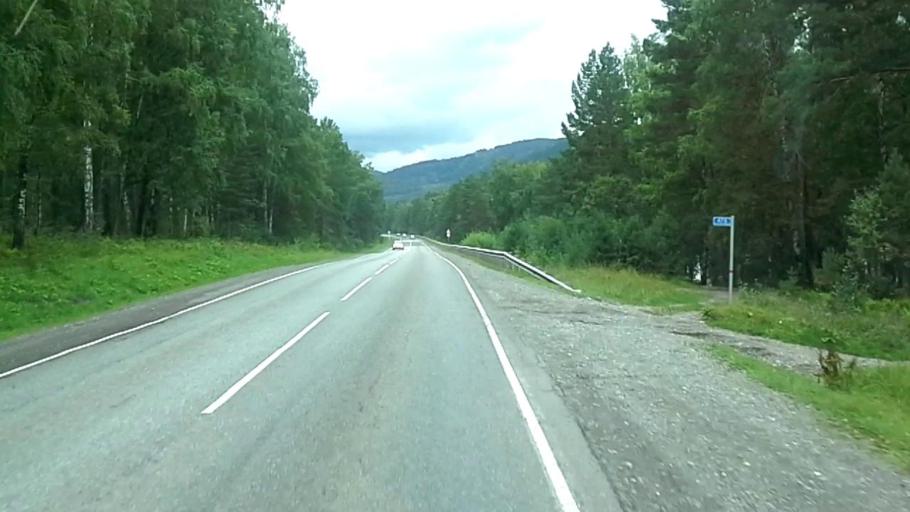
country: RU
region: Altay
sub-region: Mayminskiy Rayon
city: Manzherok
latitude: 51.8122
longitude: 85.7640
